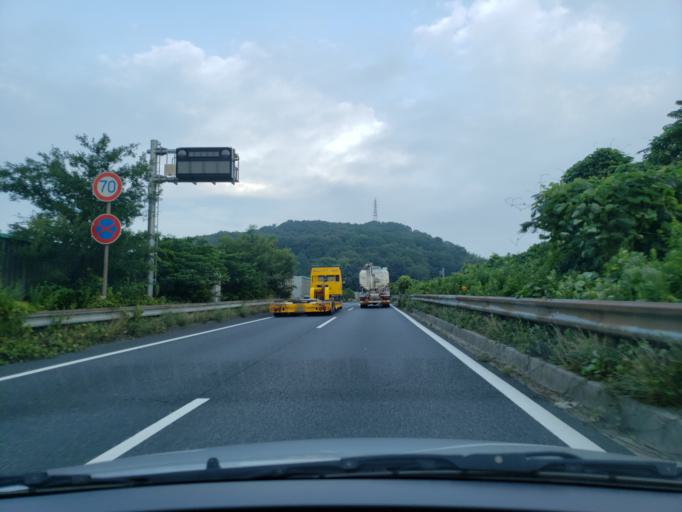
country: JP
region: Hyogo
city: Tatsunocho-tominaga
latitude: 34.8474
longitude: 134.5810
